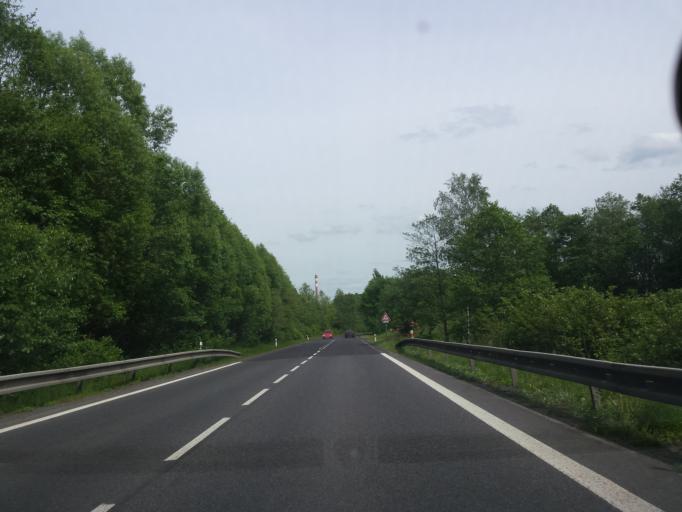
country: CZ
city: Novy Bor
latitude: 50.7506
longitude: 14.5436
